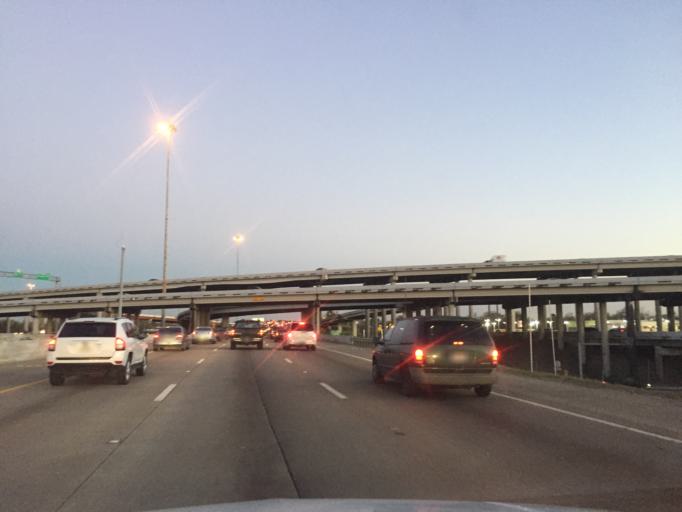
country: US
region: Texas
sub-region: Harris County
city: South Houston
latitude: 29.6980
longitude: -95.2901
